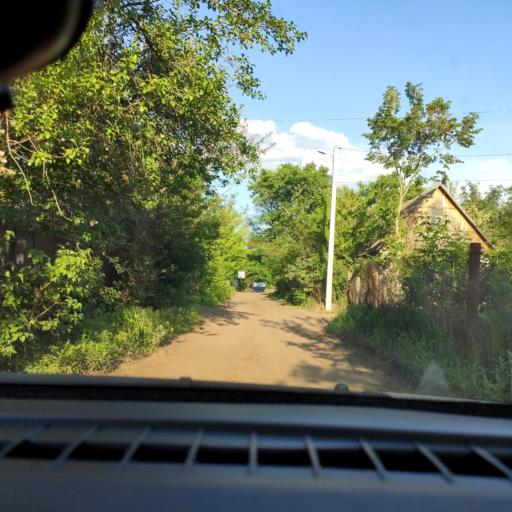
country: RU
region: Voronezj
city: Maslovka
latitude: 51.5215
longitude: 39.2378
